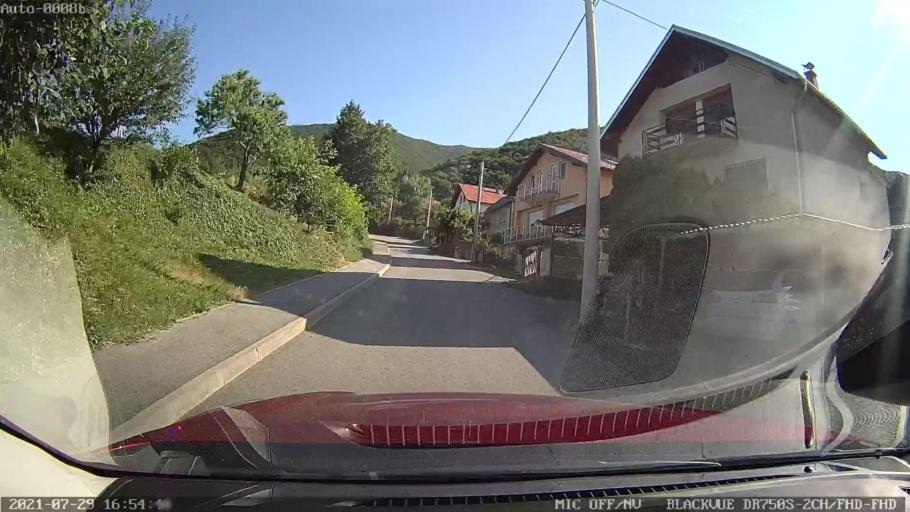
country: HR
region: Varazdinska
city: Ivanec
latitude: 46.1984
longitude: 16.1374
